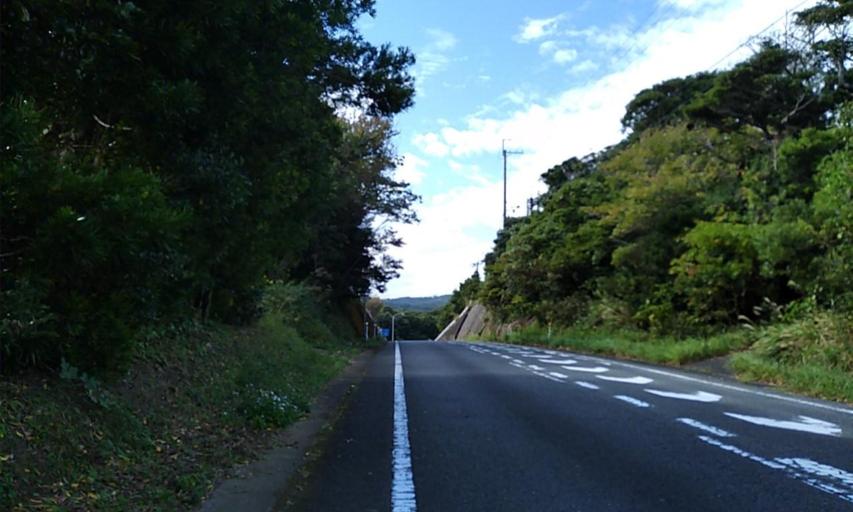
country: JP
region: Wakayama
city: Shingu
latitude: 33.4686
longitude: 135.8555
